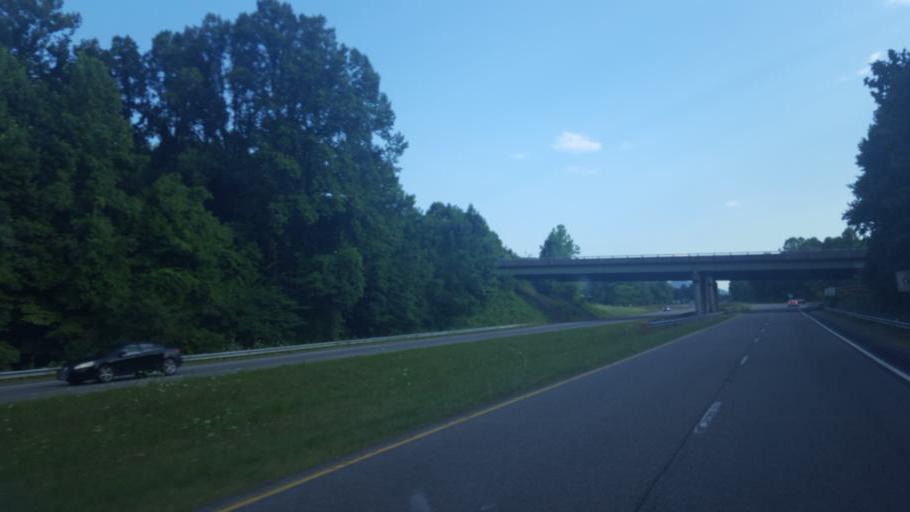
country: US
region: Virginia
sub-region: Wise County
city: Big Stone Gap
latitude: 36.8630
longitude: -82.7528
